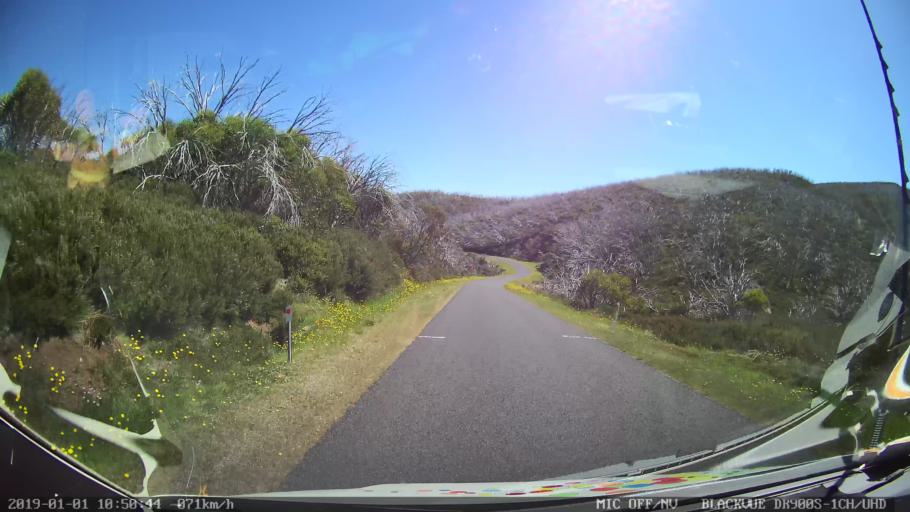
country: AU
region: New South Wales
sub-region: Snowy River
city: Jindabyne
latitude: -36.0256
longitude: 148.3715
